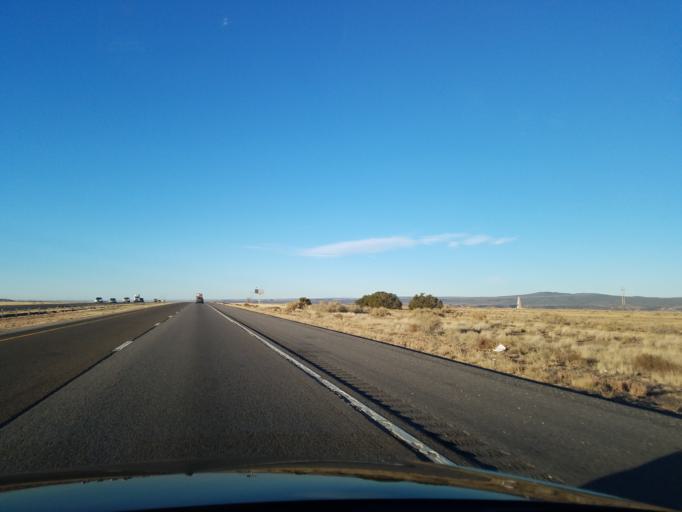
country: US
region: New Mexico
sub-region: Sandoval County
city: Santo Domingo Pueblo
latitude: 35.4514
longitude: -106.3508
